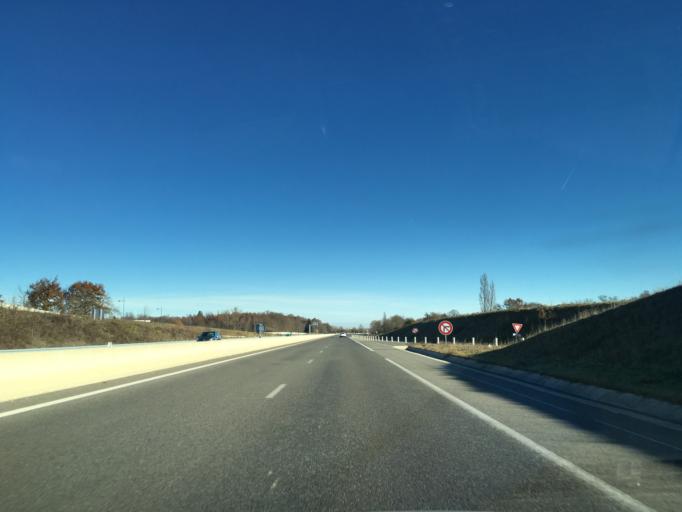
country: FR
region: Midi-Pyrenees
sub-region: Departement des Hautes-Pyrenees
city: Ossun
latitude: 43.1722
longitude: 0.0002
